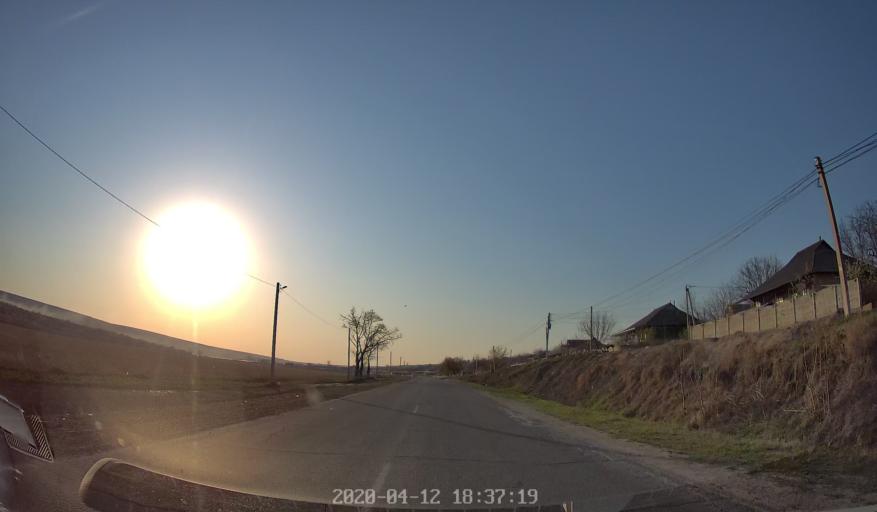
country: MD
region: Chisinau
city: Vadul lui Voda
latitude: 47.1202
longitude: 29.0172
